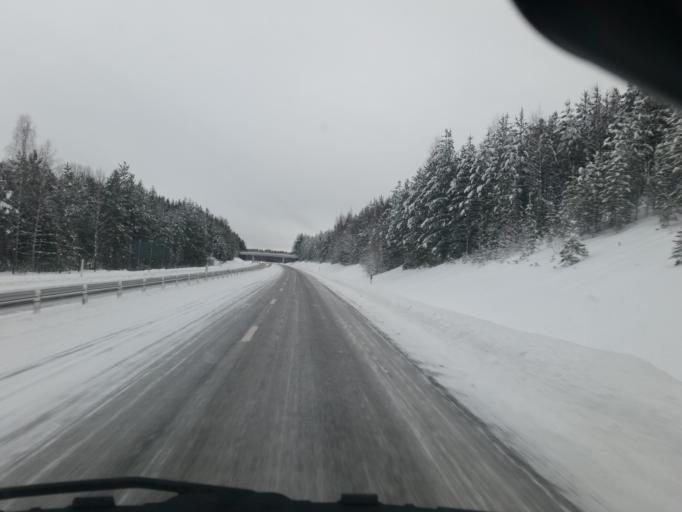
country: SE
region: Norrbotten
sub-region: Pitea Kommun
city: Bergsviken
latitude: 65.3043
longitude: 21.4107
